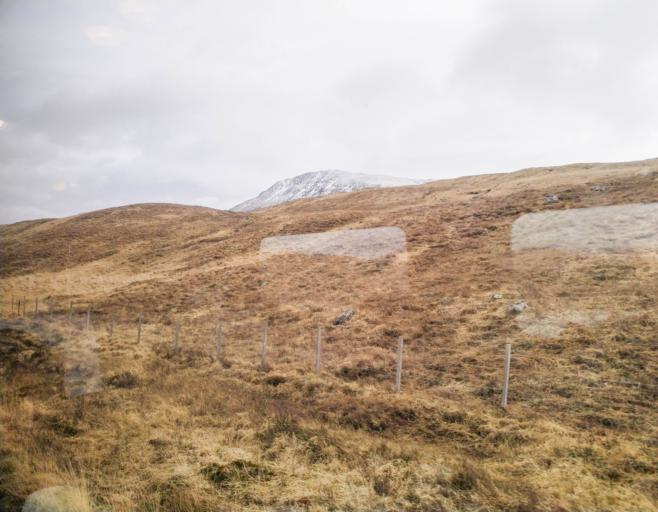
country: GB
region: Scotland
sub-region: Highland
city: Spean Bridge
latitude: 56.5498
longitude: -4.7494
